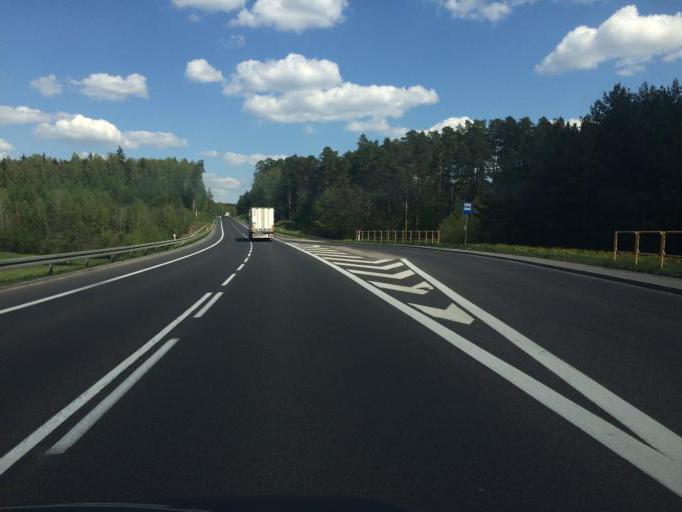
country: PL
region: Warmian-Masurian Voivodeship
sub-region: Powiat olsztynski
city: Gietrzwald
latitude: 53.7601
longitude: 20.2972
